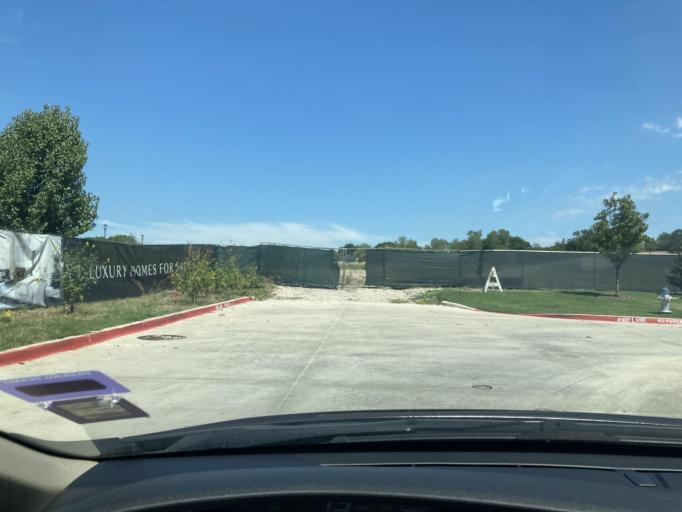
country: US
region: Texas
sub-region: Dallas County
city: University Park
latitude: 32.8825
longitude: -96.7738
